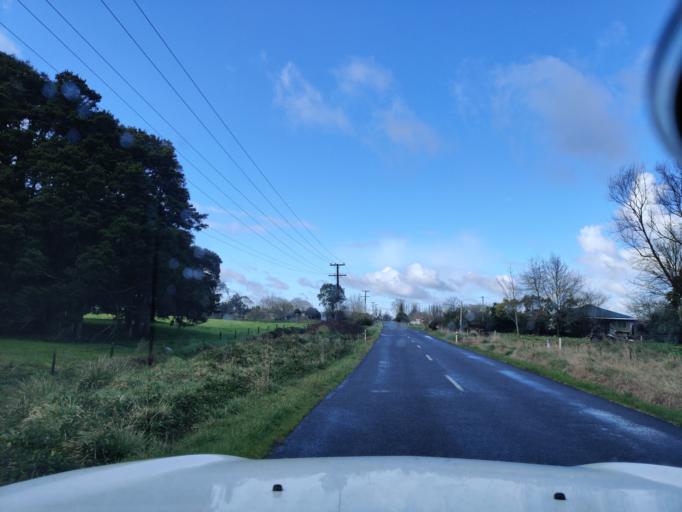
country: NZ
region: Waikato
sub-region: Waikato District
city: Ngaruawahia
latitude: -37.5711
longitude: 175.2649
